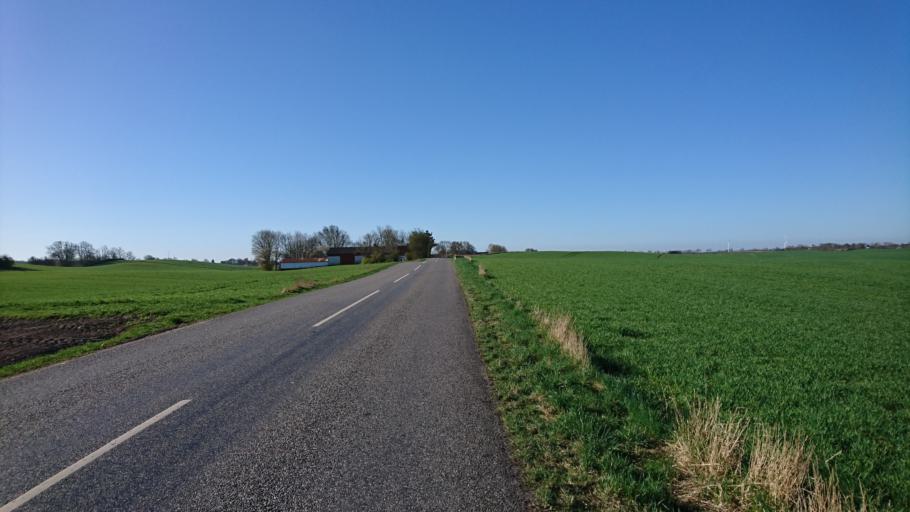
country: DK
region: Capital Region
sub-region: Frederikssund Kommune
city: Skibby
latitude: 55.7345
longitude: 11.9289
